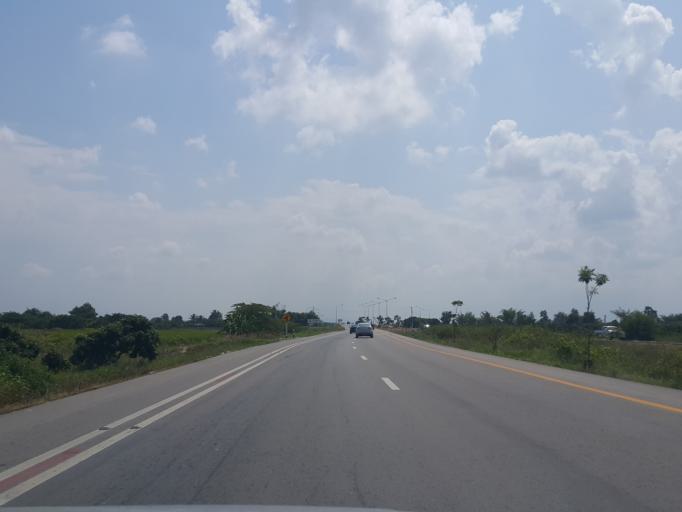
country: TH
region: Chiang Mai
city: San Pa Tong
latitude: 18.5850
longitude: 98.8404
